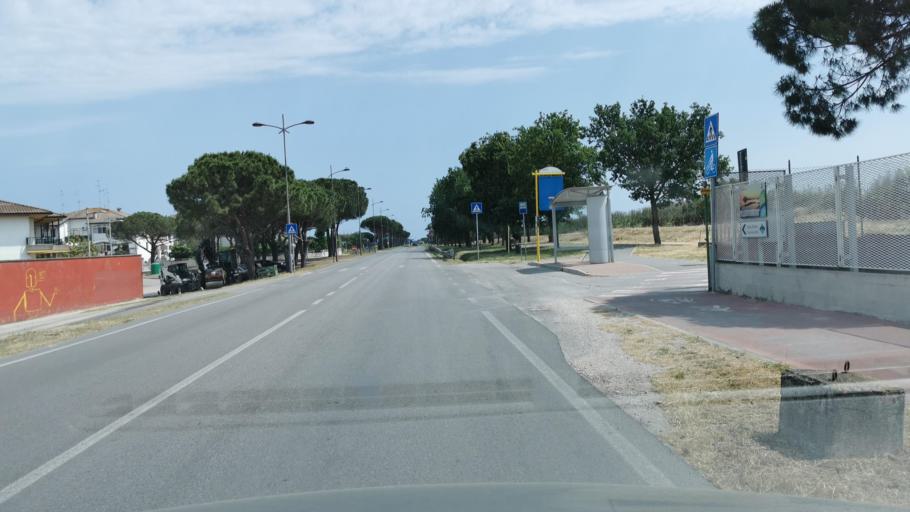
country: IT
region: Emilia-Romagna
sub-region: Provincia di Ferrara
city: Comacchio
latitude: 44.6899
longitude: 12.1880
